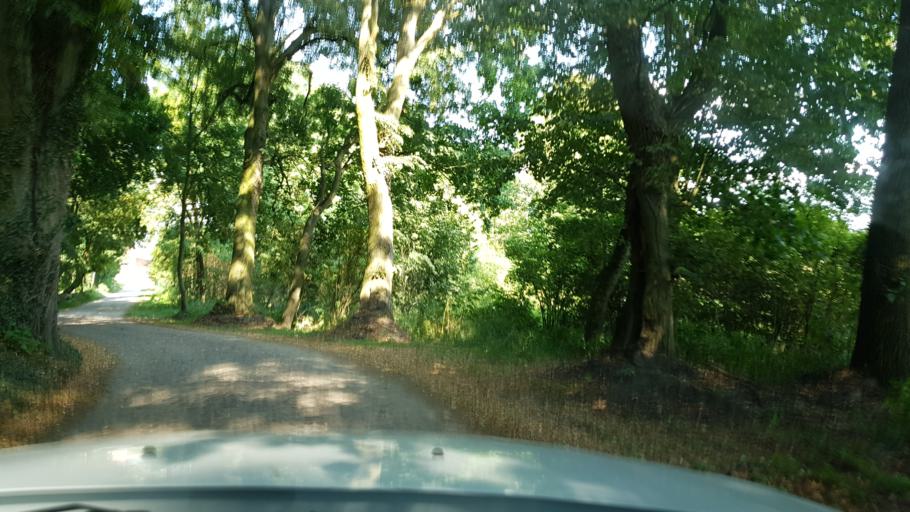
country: PL
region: West Pomeranian Voivodeship
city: Trzcinsko Zdroj
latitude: 52.9086
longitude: 14.5915
